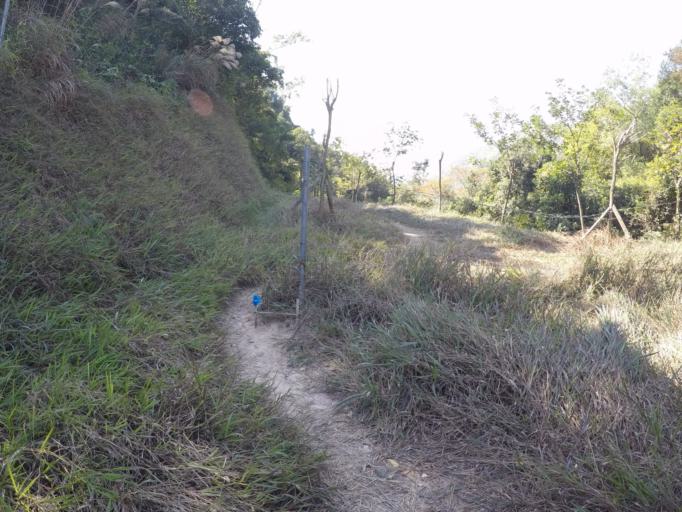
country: CN
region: Guangdong
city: Huancheng
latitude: 22.4664
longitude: 113.4185
